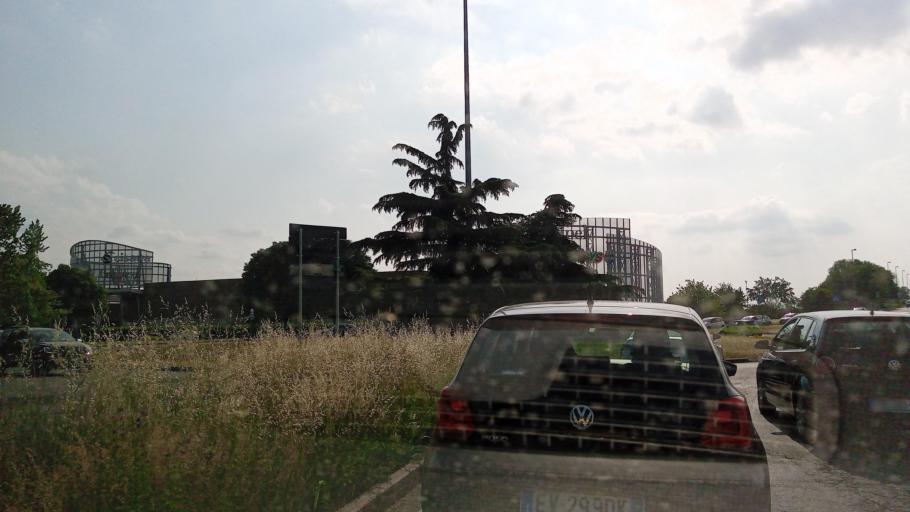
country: IT
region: Piedmont
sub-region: Provincia di Torino
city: Lesna
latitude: 45.0595
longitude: 7.6156
